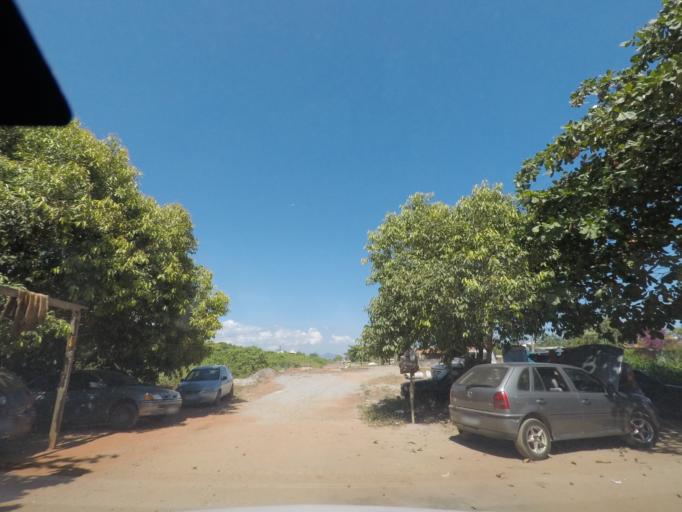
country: BR
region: Rio de Janeiro
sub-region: Marica
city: Marica
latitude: -22.9714
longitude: -42.9141
